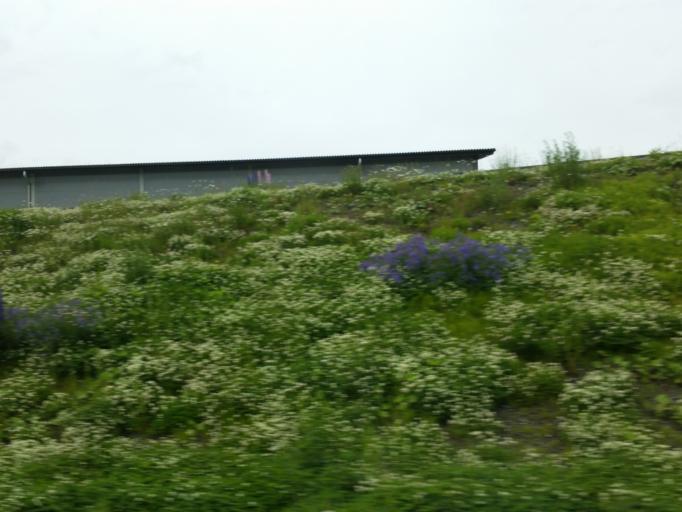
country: FI
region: Northern Savo
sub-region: Kuopio
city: Kuopio
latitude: 62.9572
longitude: 27.6887
